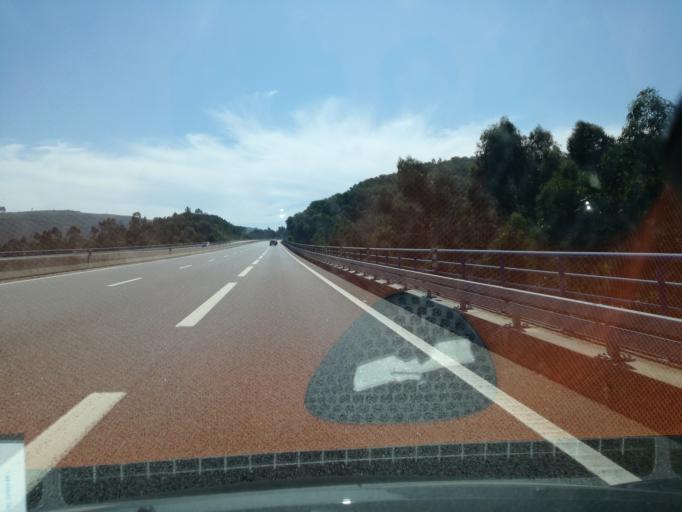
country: PT
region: Viana do Castelo
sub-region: Caminha
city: Vila Praia de Ancora
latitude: 41.7992
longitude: -8.7978
